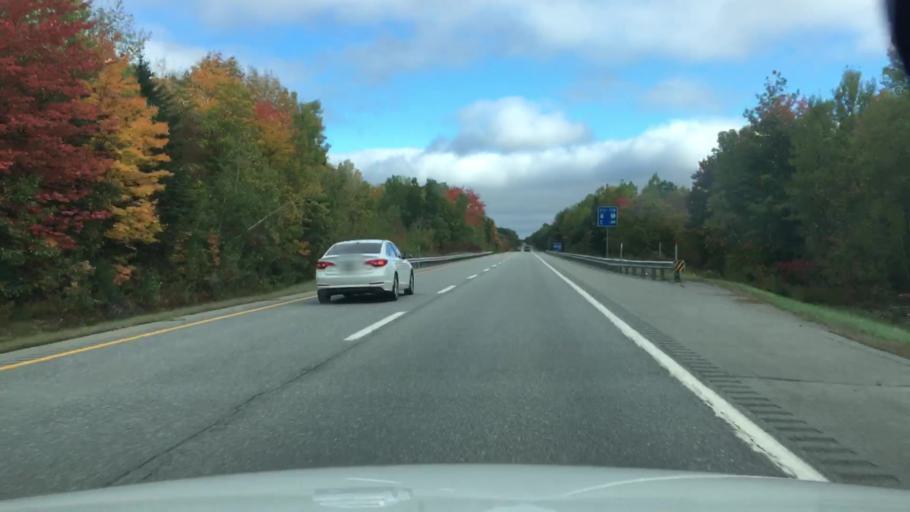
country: US
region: Maine
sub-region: Penobscot County
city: Carmel
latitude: 44.7670
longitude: -68.9957
